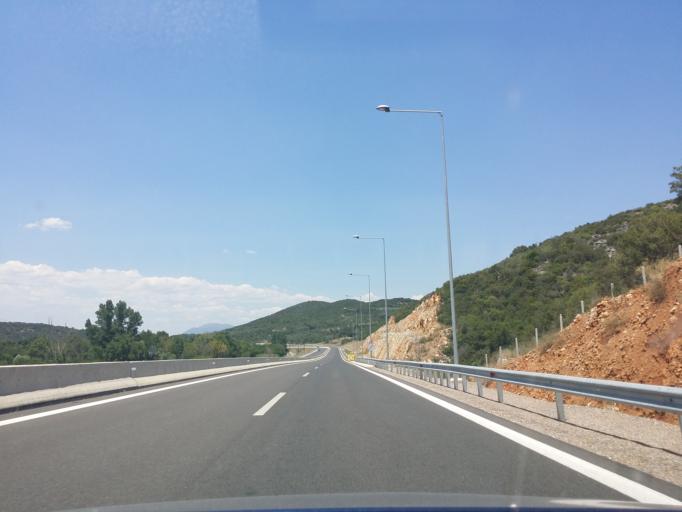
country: GR
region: Peloponnese
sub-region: Nomos Lakonias
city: Magoula
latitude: 37.1525
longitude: 22.3845
